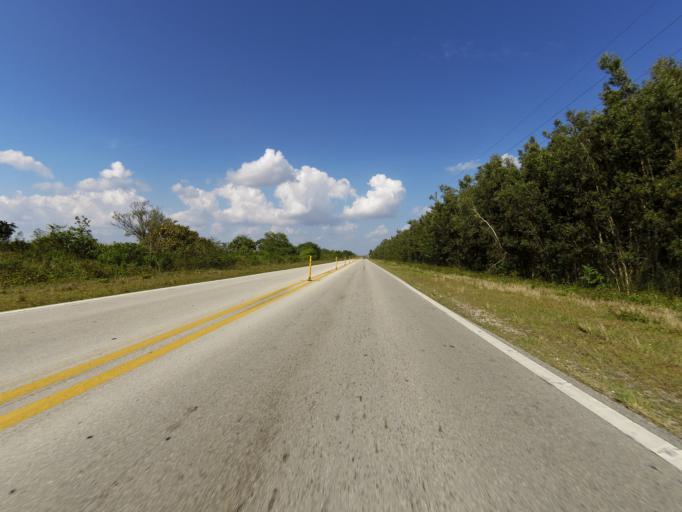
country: US
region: Florida
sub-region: Miami-Dade County
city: Palm Springs North
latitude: 25.9213
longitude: -80.4578
